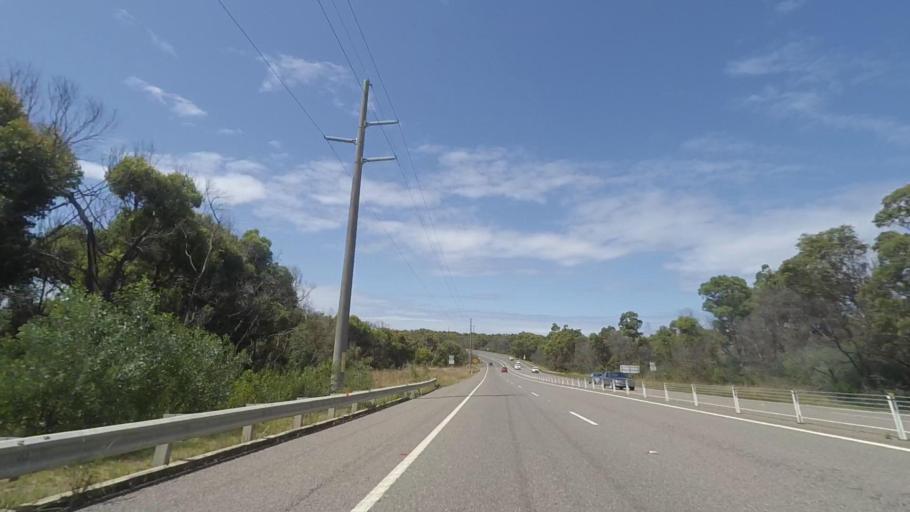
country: AU
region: New South Wales
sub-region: Wyong Shire
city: Kingfisher Shores
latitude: -33.1649
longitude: 151.6104
